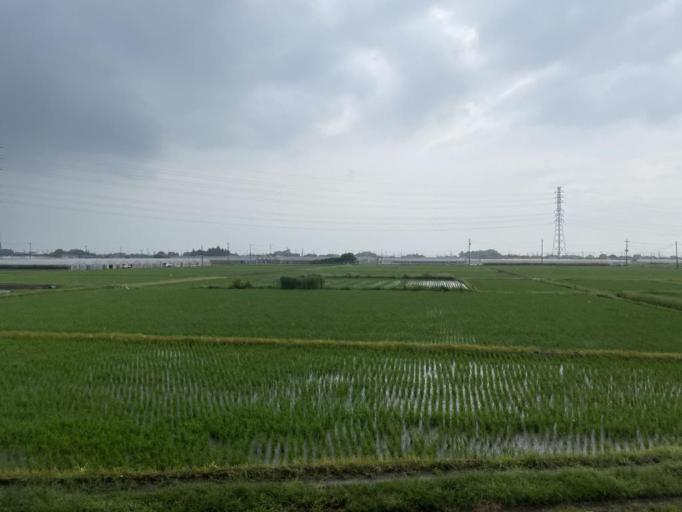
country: JP
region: Tochigi
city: Ashikaga
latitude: 36.2932
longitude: 139.4681
